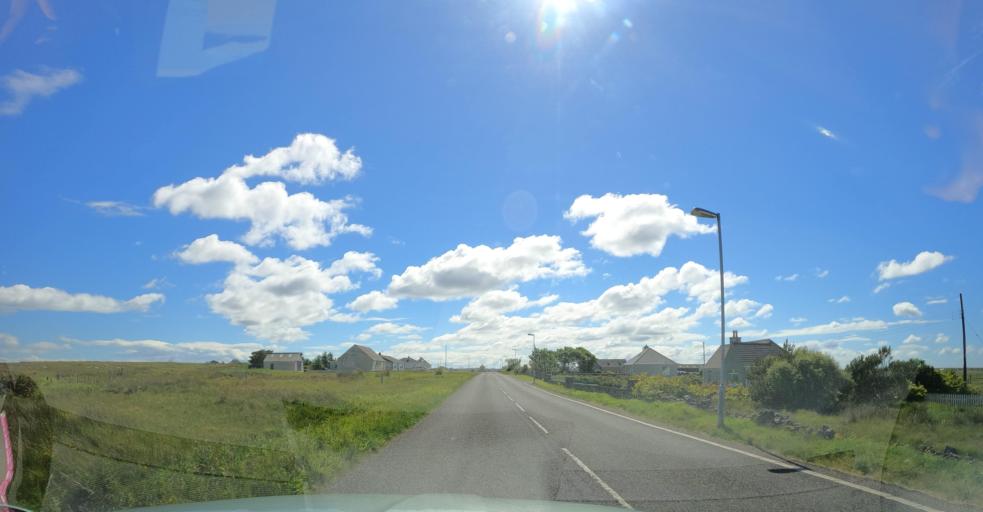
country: GB
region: Scotland
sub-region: Eilean Siar
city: Isle of Lewis
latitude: 58.3611
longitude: -6.5107
